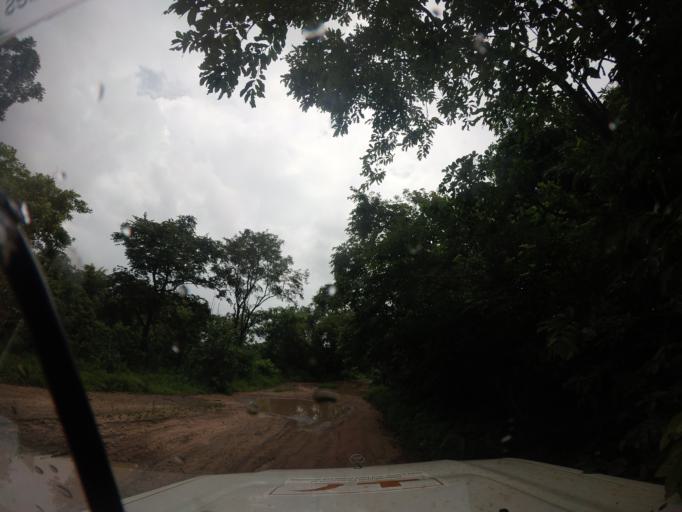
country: SL
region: Northern Province
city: Loma
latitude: 9.8680
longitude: -12.4156
